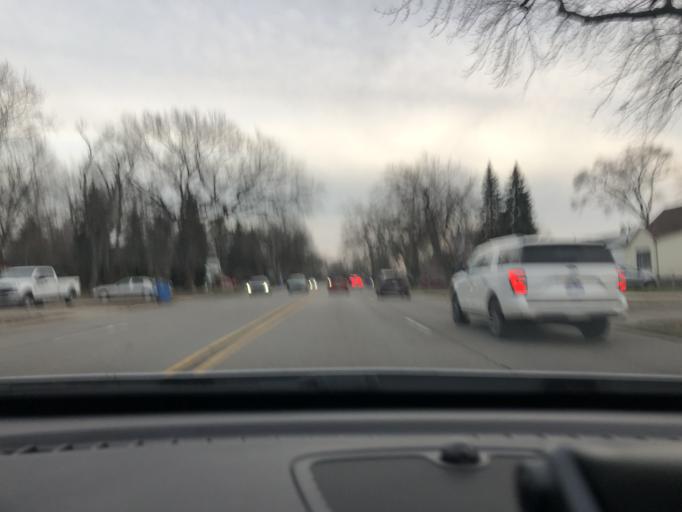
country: US
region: Michigan
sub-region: Wayne County
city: Allen Park
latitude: 42.2750
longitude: -83.2313
